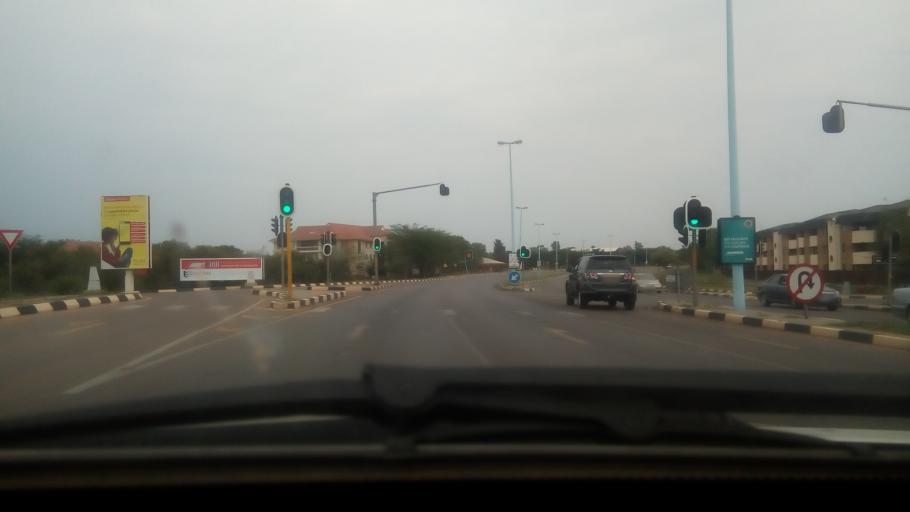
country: BW
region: South East
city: Gaborone
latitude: -24.6753
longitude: 25.9298
